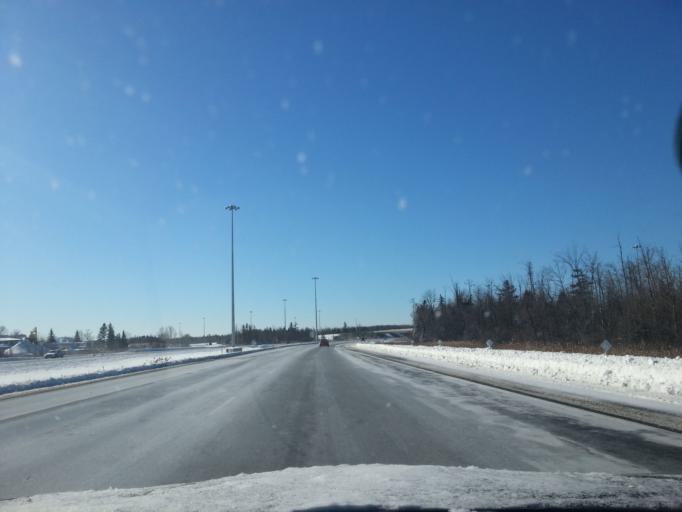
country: CA
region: Ontario
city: Bells Corners
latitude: 45.2748
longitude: -75.9672
